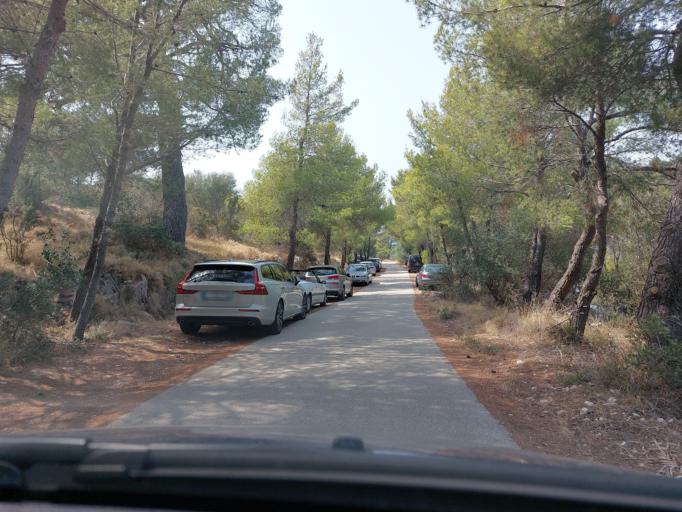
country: HR
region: Dubrovacko-Neretvanska
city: Smokvica
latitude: 42.7266
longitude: 16.8851
